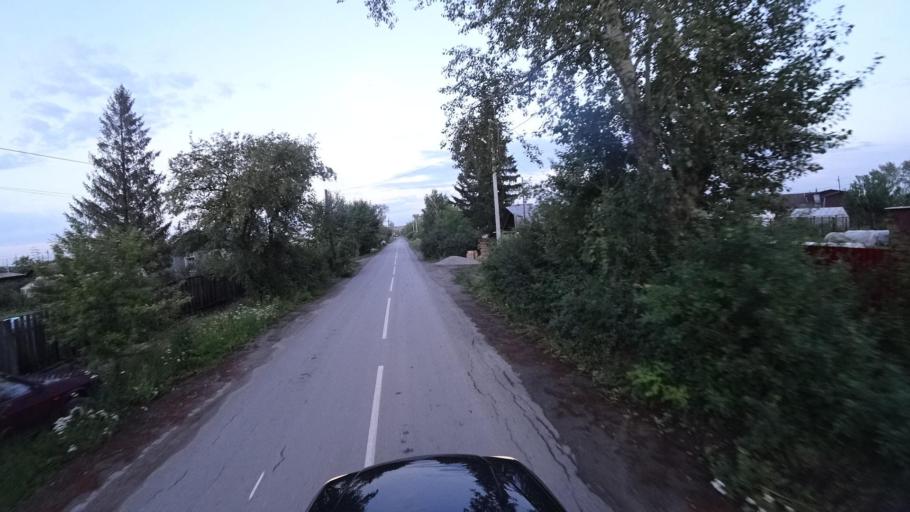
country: RU
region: Sverdlovsk
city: Kamyshlov
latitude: 56.8501
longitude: 62.7304
